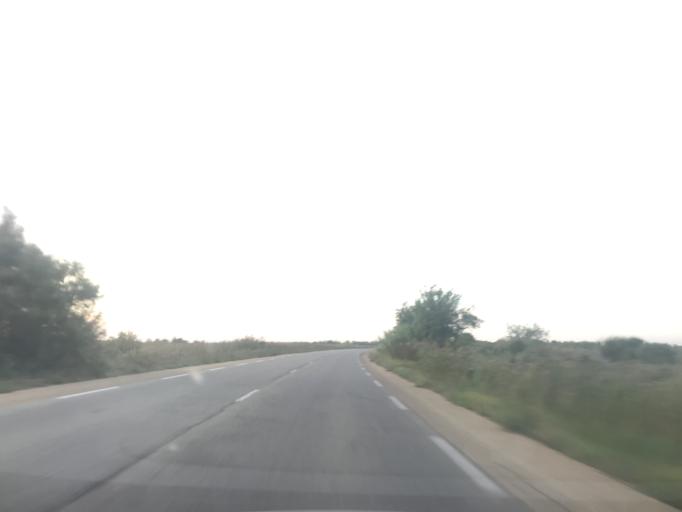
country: FR
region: Provence-Alpes-Cote d'Azur
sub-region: Departement des Bouches-du-Rhone
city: Saintes-Maries-de-la-Mer
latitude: 43.5096
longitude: 4.3992
